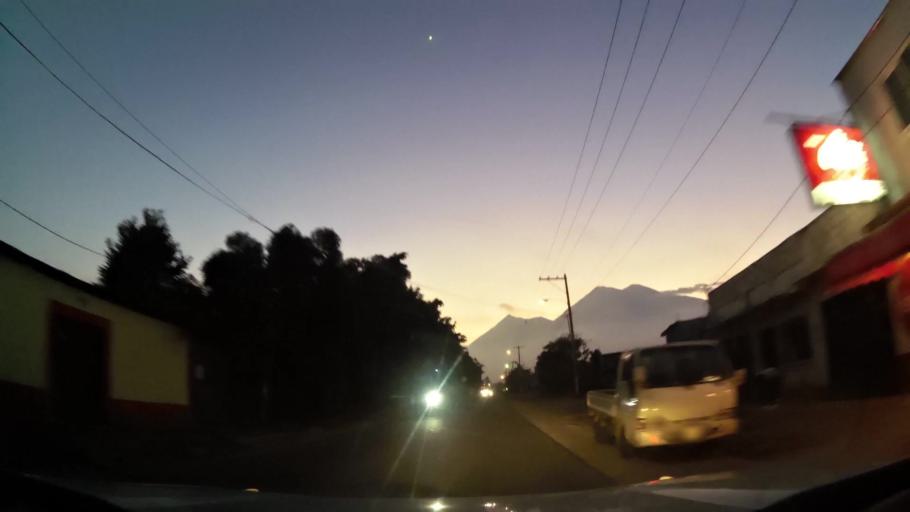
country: GT
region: Sacatepequez
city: Ciudad Vieja
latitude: 14.5216
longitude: -90.7711
